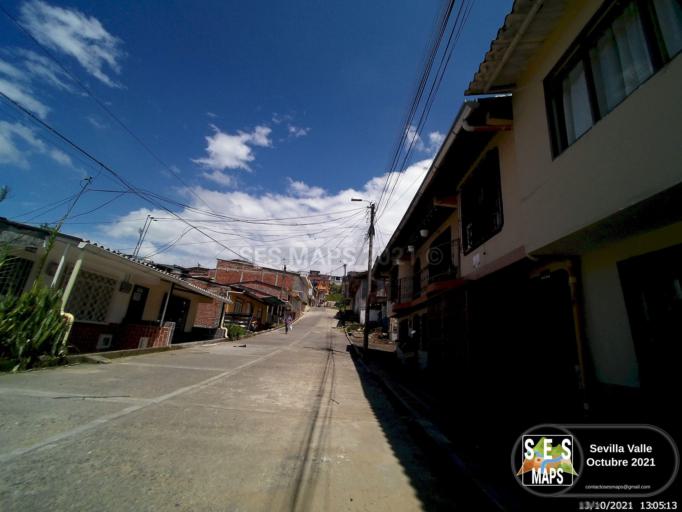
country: CO
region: Valle del Cauca
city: Sevilla
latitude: 4.2662
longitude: -75.9296
